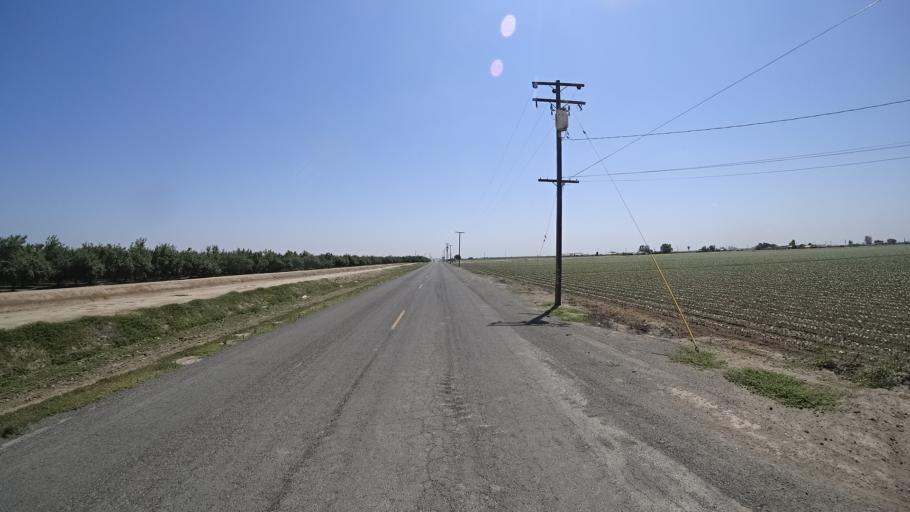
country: US
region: California
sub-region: Kings County
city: Home Garden
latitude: 36.2840
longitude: -119.6248
